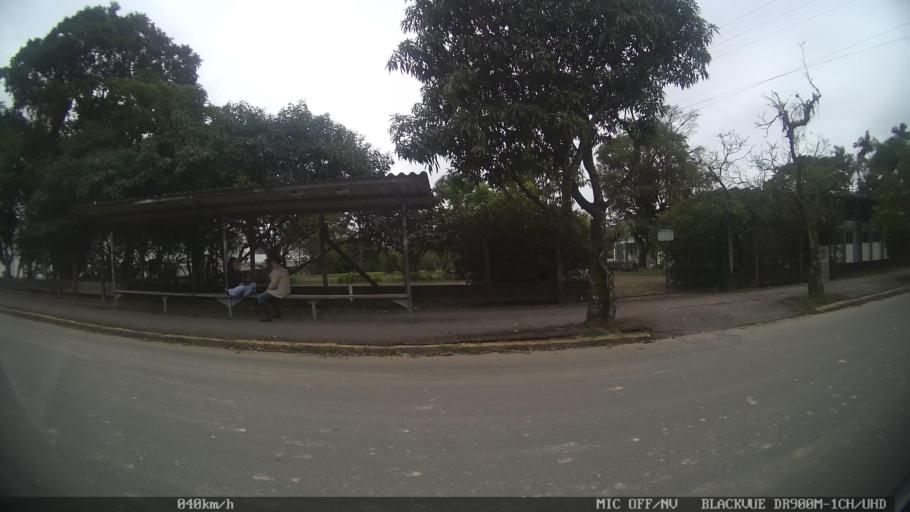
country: BR
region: Santa Catarina
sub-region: Joinville
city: Joinville
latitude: -26.2602
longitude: -48.8547
